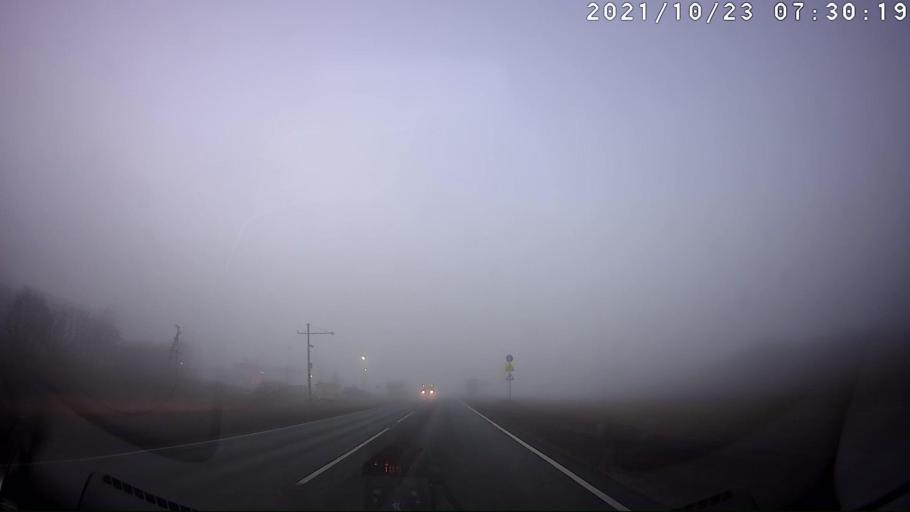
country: RU
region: Saratov
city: Alekseyevka
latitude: 52.2972
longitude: 47.9281
